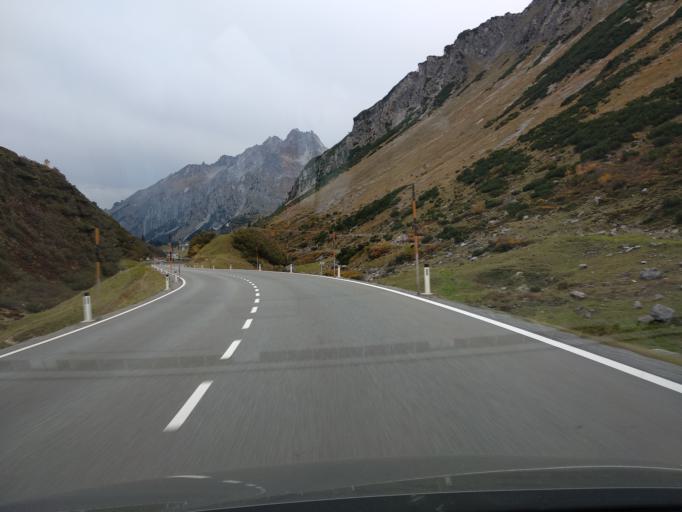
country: AT
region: Tyrol
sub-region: Politischer Bezirk Landeck
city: Sankt Anton am Arlberg
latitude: 47.1360
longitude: 10.2010
